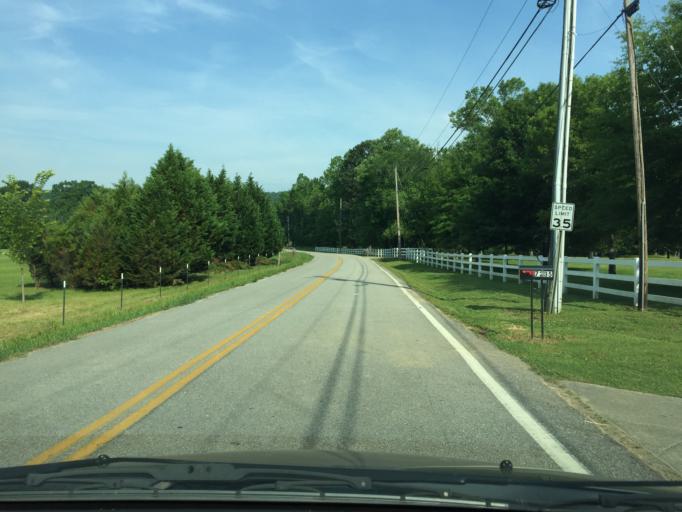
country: US
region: Tennessee
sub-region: Hamilton County
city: Collegedale
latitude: 35.0891
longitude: -85.0130
